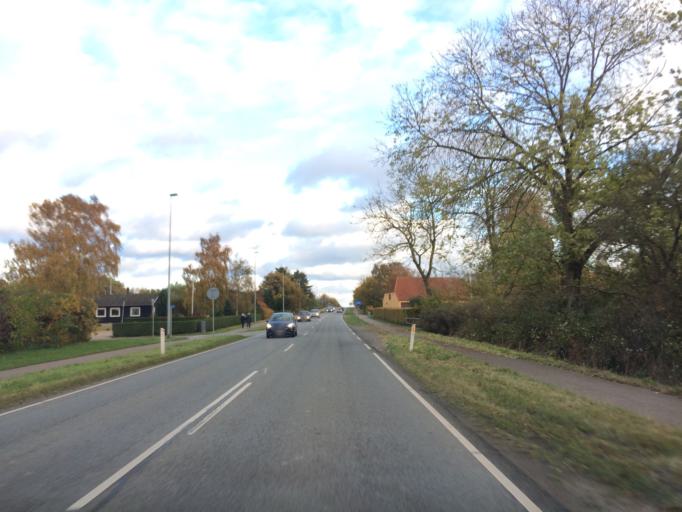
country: DK
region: South Denmark
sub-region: Sonderborg Kommune
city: Nordborg
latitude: 55.0424
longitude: 9.7950
